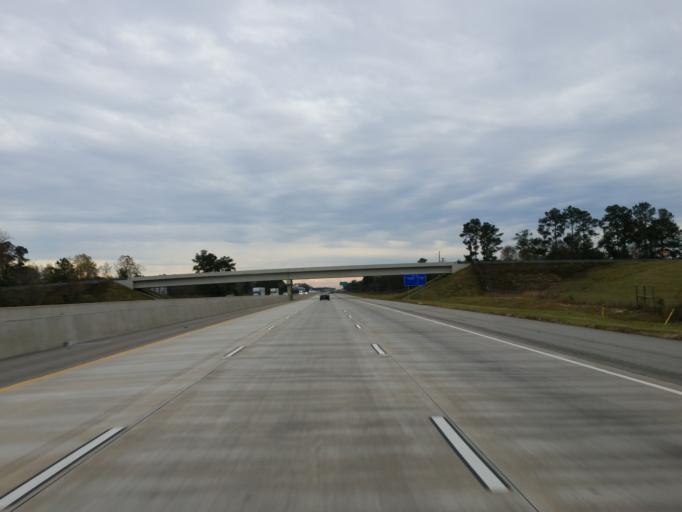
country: US
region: Georgia
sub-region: Cook County
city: Sparks
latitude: 31.2381
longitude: -83.4652
